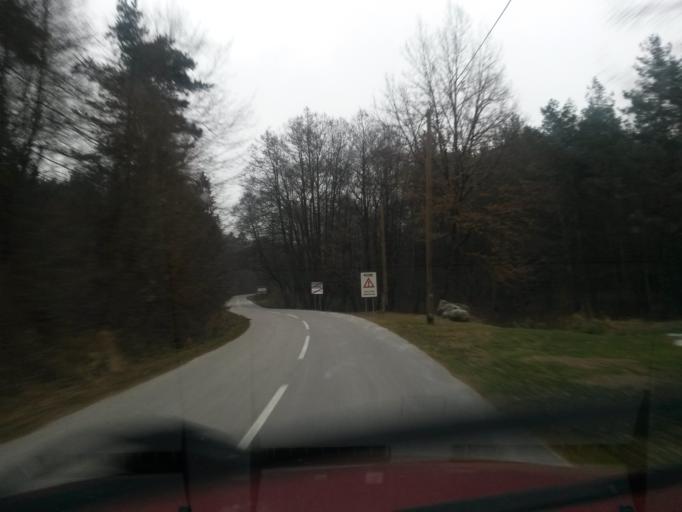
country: SK
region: Kosicky
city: Roznava
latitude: 48.6562
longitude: 20.6075
